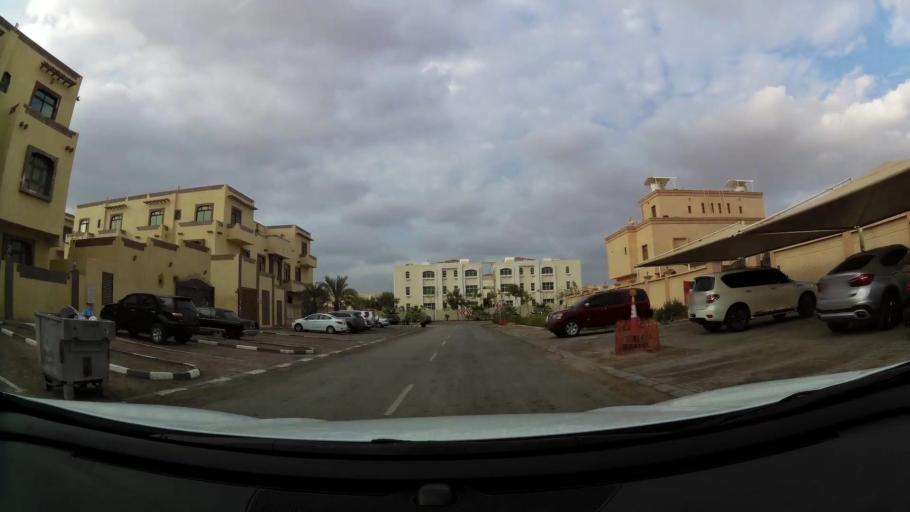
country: AE
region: Abu Dhabi
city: Abu Dhabi
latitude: 24.3560
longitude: 54.5515
